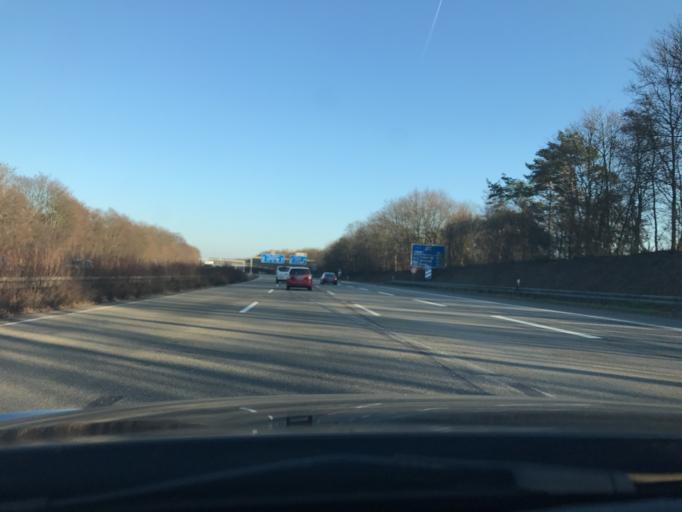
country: DE
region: North Rhine-Westphalia
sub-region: Regierungsbezirk Dusseldorf
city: Meerbusch
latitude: 51.2694
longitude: 6.7312
